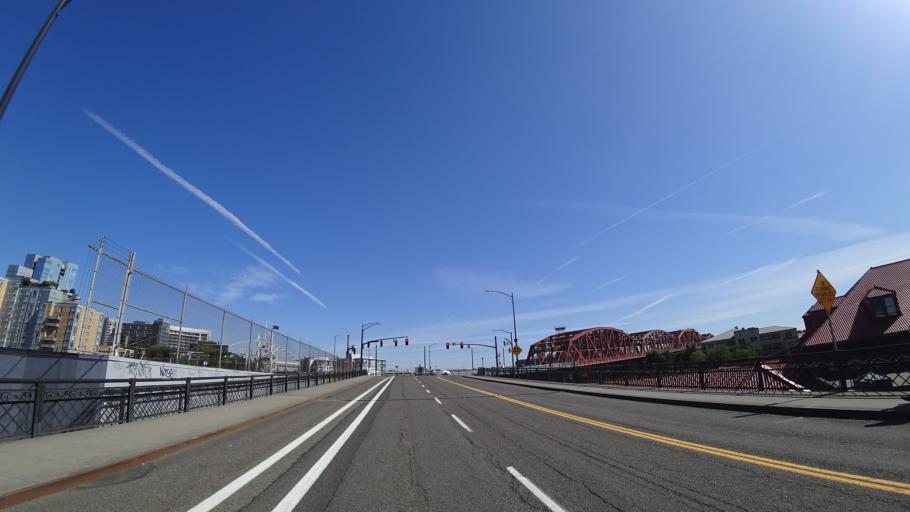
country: US
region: Oregon
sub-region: Multnomah County
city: Portland
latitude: 45.5291
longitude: -122.6777
